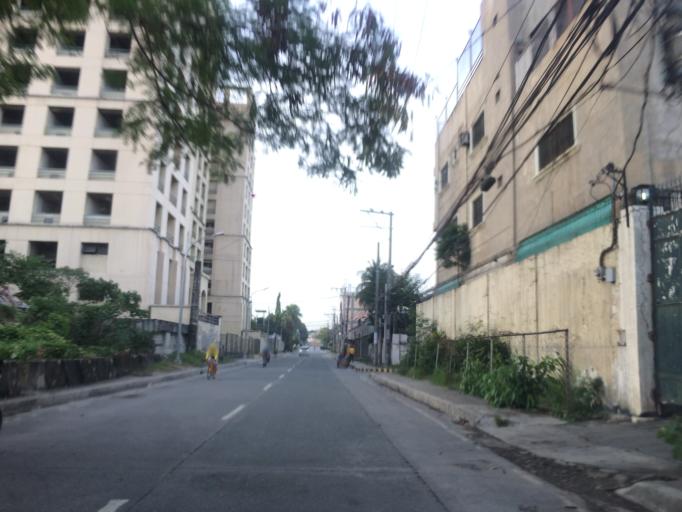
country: PH
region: Calabarzon
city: Del Monte
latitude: 14.6322
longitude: 121.0048
